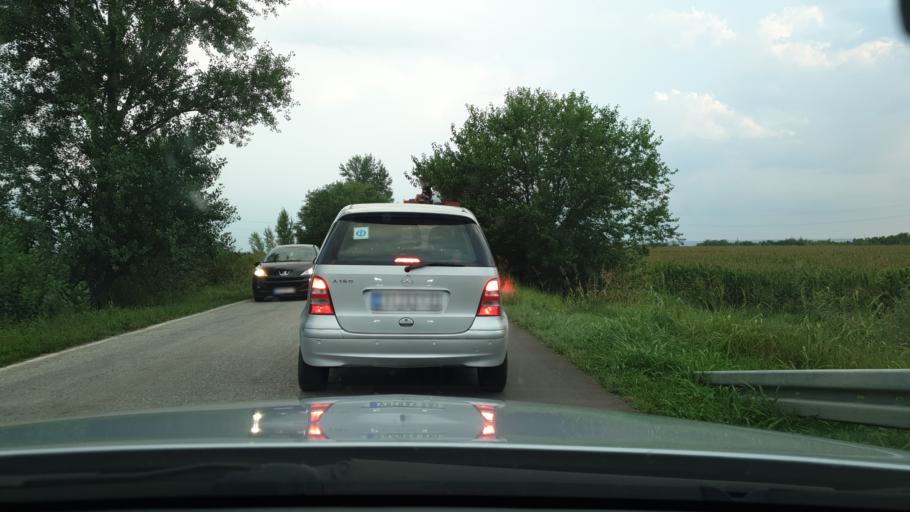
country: RS
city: Pavlis
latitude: 45.0325
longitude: 21.2801
